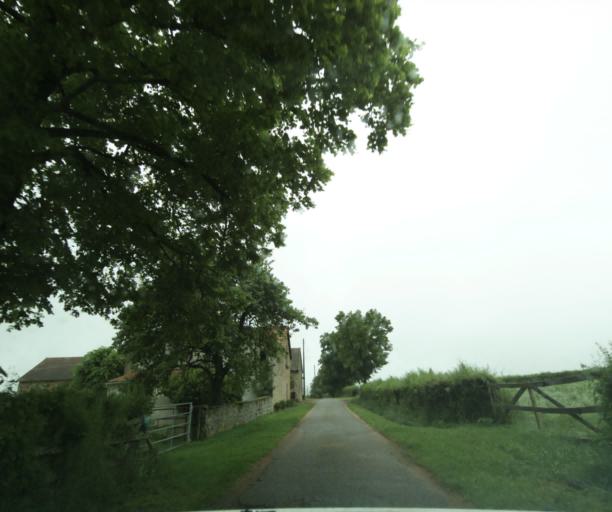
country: FR
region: Bourgogne
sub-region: Departement de Saone-et-Loire
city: Charolles
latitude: 46.4331
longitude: 4.3675
